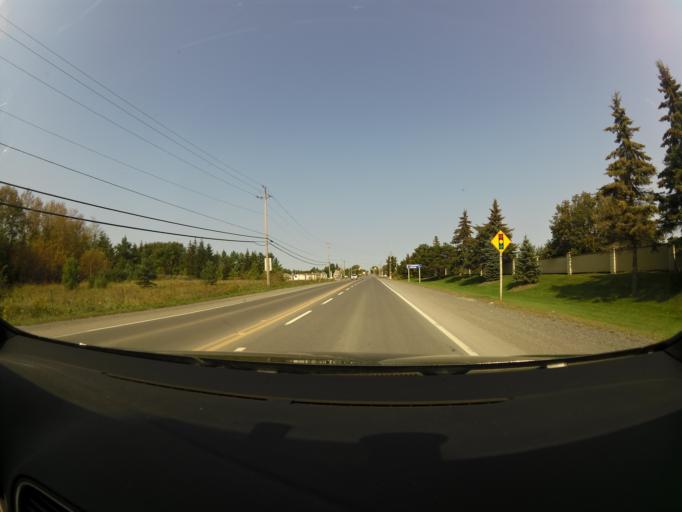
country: CA
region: Ontario
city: Bells Corners
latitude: 45.2916
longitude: -75.9701
